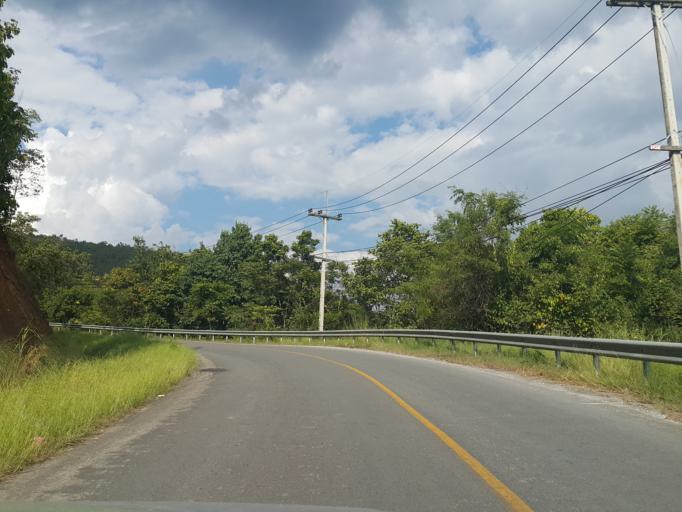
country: TH
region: Chiang Mai
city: Mae Chaem
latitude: 18.5386
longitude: 98.3732
